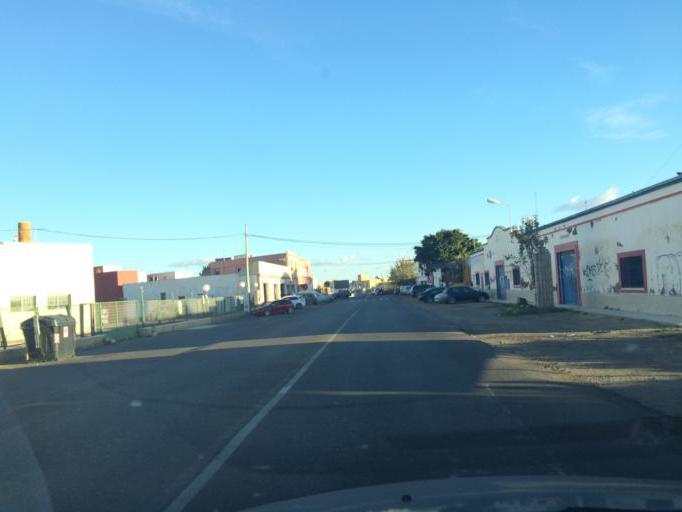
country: ES
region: Andalusia
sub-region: Provincia de Almeria
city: Almeria
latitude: 36.8421
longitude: -2.4260
